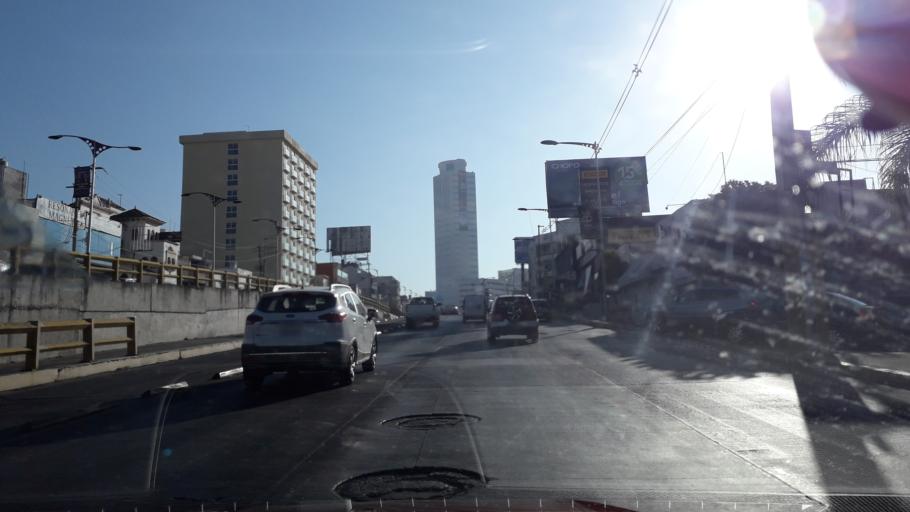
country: MX
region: Puebla
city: Puebla
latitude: 19.0514
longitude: -98.2263
